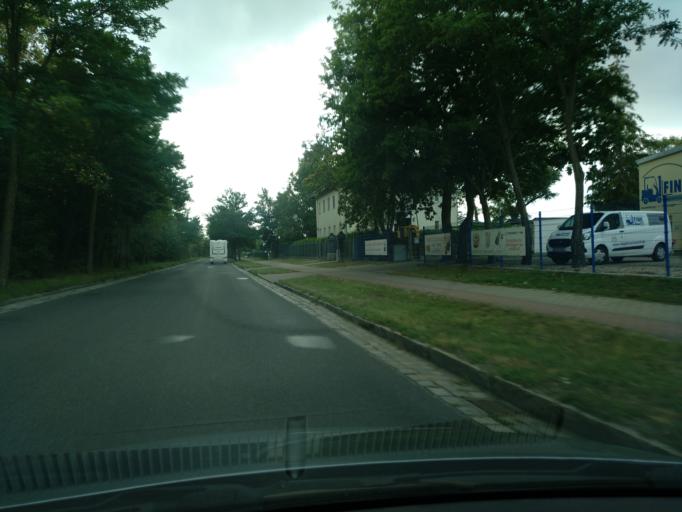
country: DE
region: Brandenburg
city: Petershagen
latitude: 52.4881
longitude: 13.7837
